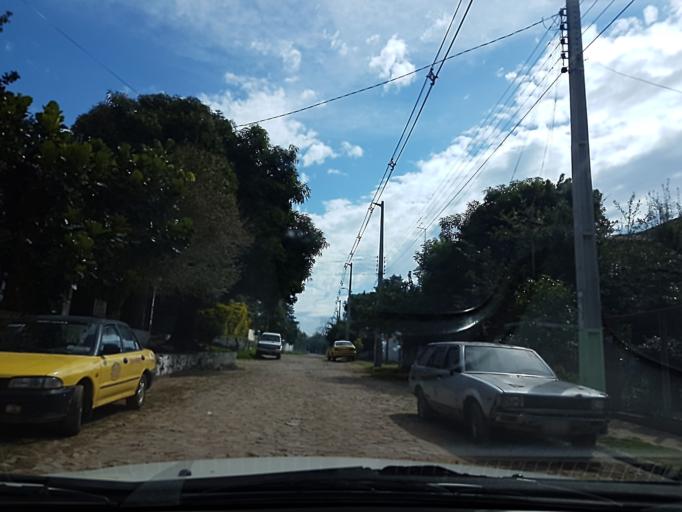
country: PY
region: Central
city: Colonia Mariano Roque Alonso
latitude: -25.2278
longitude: -57.5599
